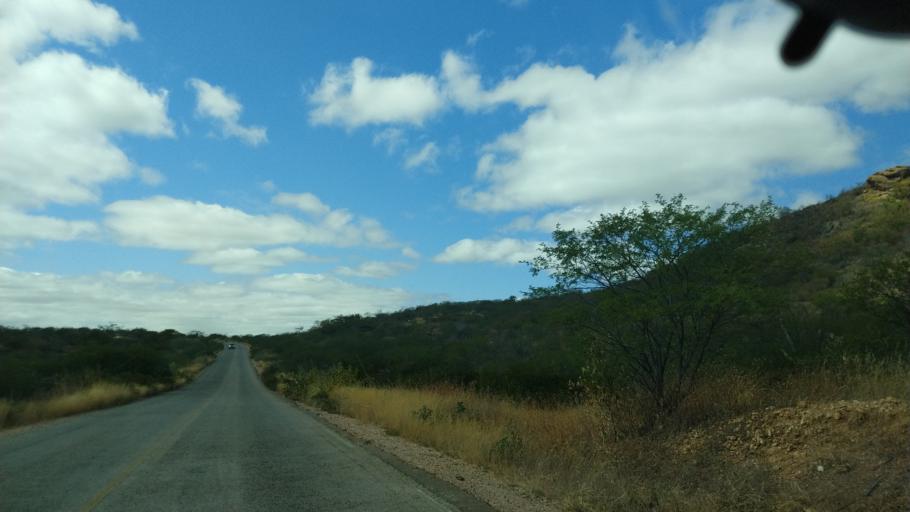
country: BR
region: Rio Grande do Norte
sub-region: Currais Novos
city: Currais Novos
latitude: -6.2683
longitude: -36.5597
